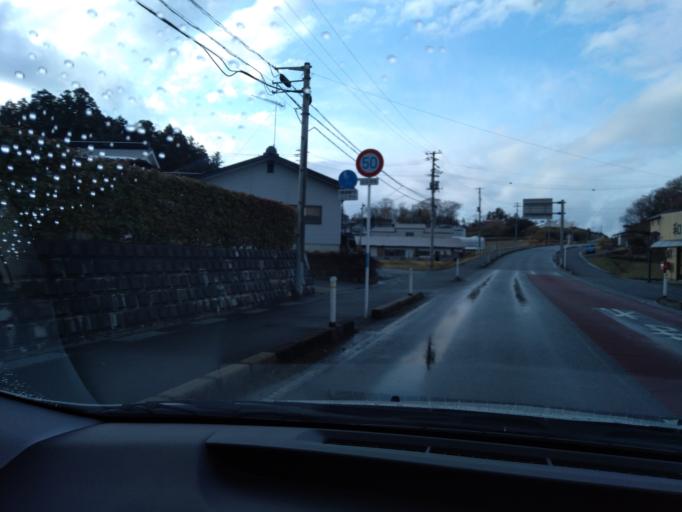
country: JP
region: Iwate
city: Ichinoseki
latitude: 38.7427
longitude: 141.1207
